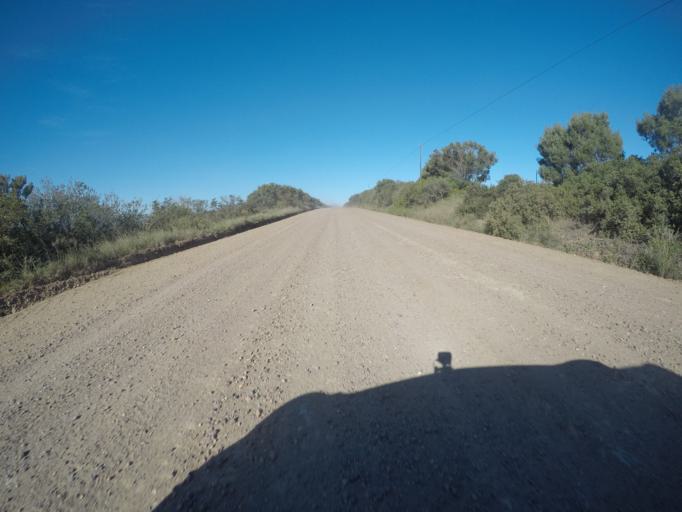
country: ZA
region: Western Cape
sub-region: Eden District Municipality
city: Mossel Bay
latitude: -34.1447
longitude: 22.0109
